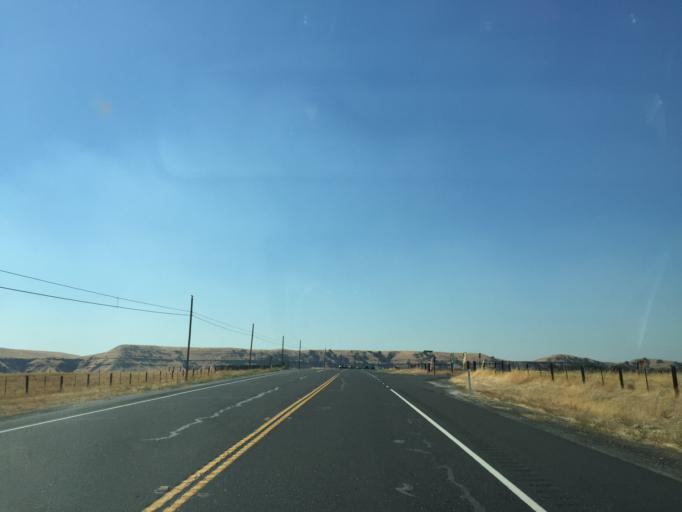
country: US
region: California
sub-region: Stanislaus County
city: East Oakdale
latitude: 37.8097
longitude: -120.6647
